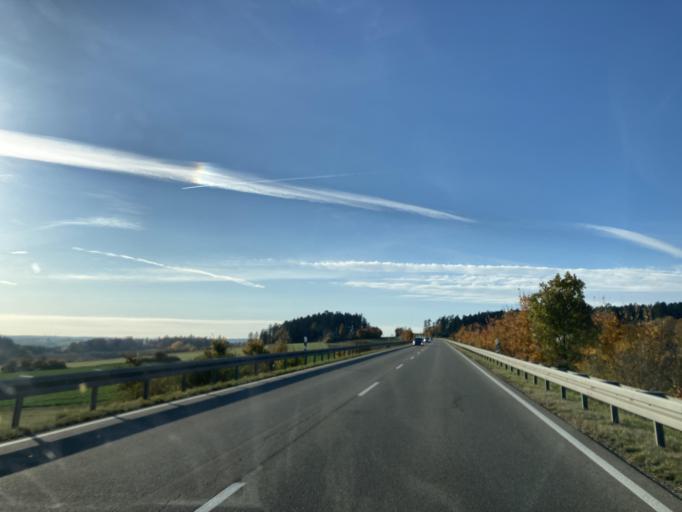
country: DE
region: Baden-Wuerttemberg
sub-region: Karlsruhe Region
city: Schopfloch
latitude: 48.4504
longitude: 8.5852
